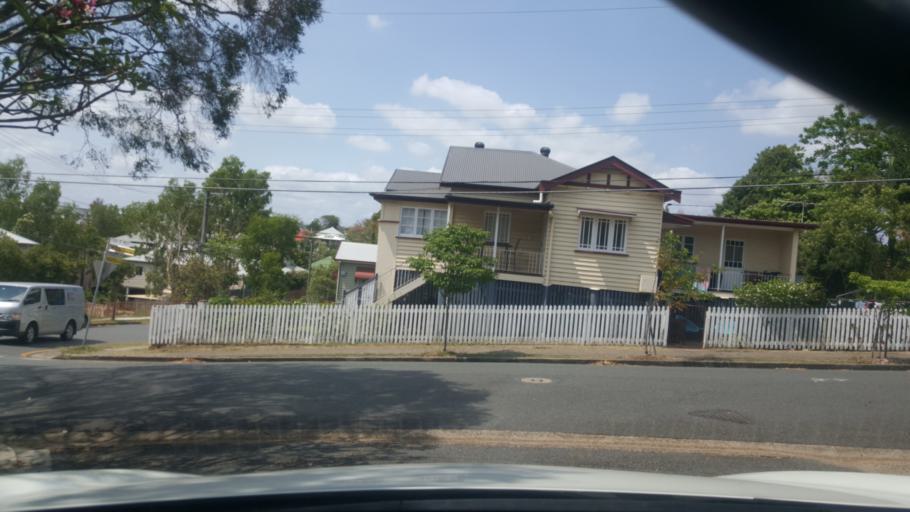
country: AU
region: Queensland
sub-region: Brisbane
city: Woolloongabba
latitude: -27.4913
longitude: 153.0258
